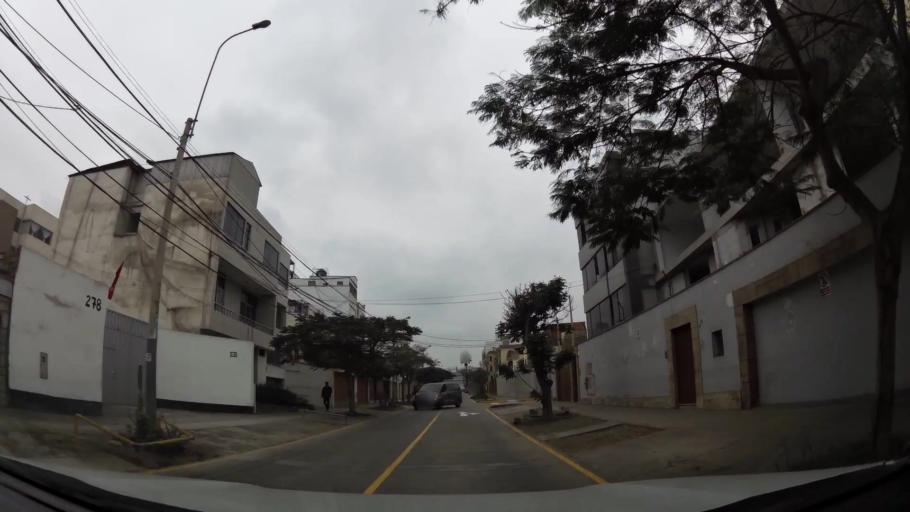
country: PE
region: Lima
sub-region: Lima
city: San Luis
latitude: -12.0914
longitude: -77.0074
